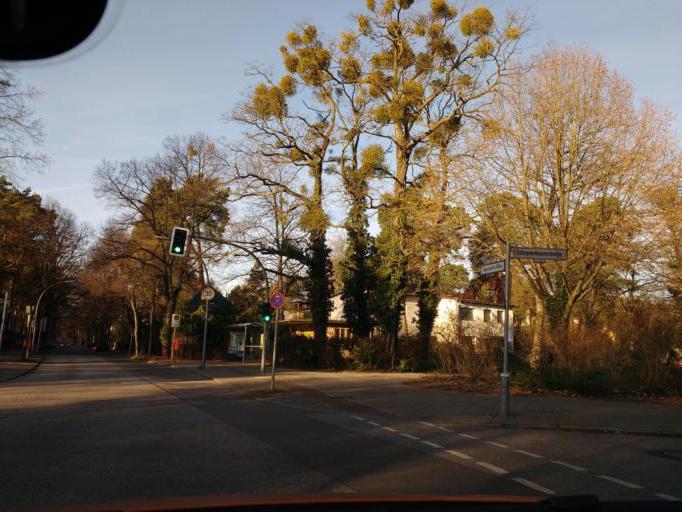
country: DE
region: Berlin
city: Nikolassee
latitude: 52.4340
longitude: 13.2122
